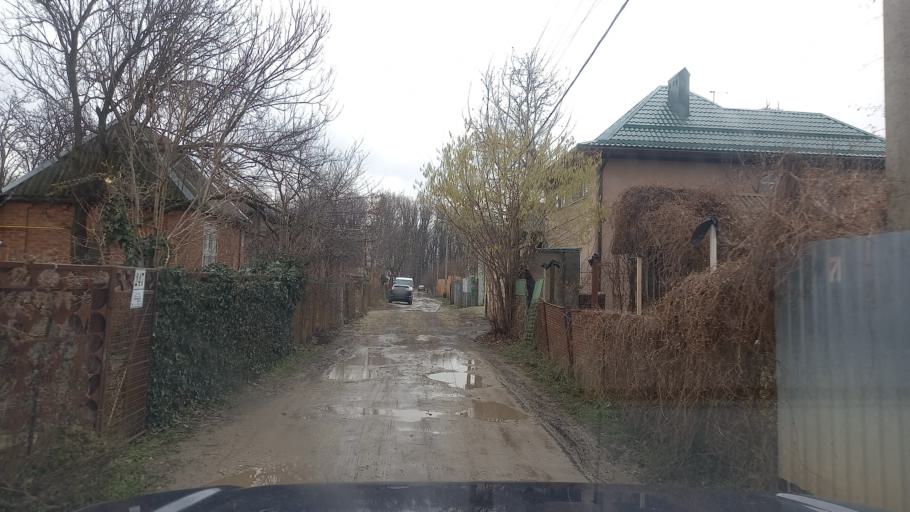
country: RU
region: Krasnodarskiy
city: Pashkovskiy
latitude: 45.0538
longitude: 39.1780
